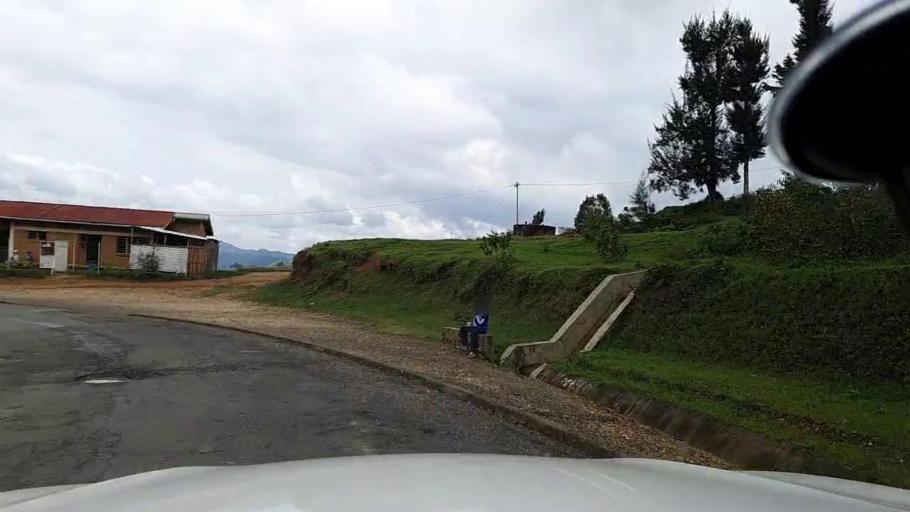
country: RW
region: Western Province
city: Kibuye
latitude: -2.0647
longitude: 29.5399
